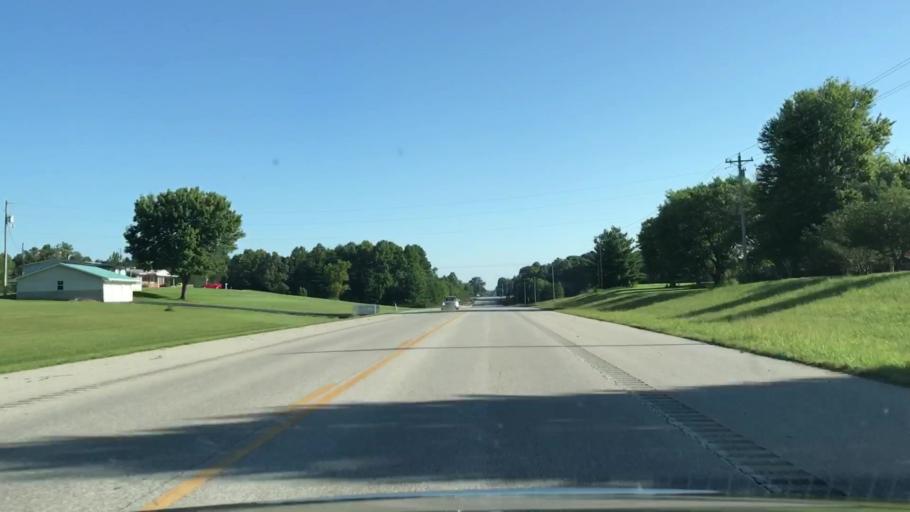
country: US
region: Tennessee
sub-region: Putnam County
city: Baxter
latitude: 36.2386
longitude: -85.6170
